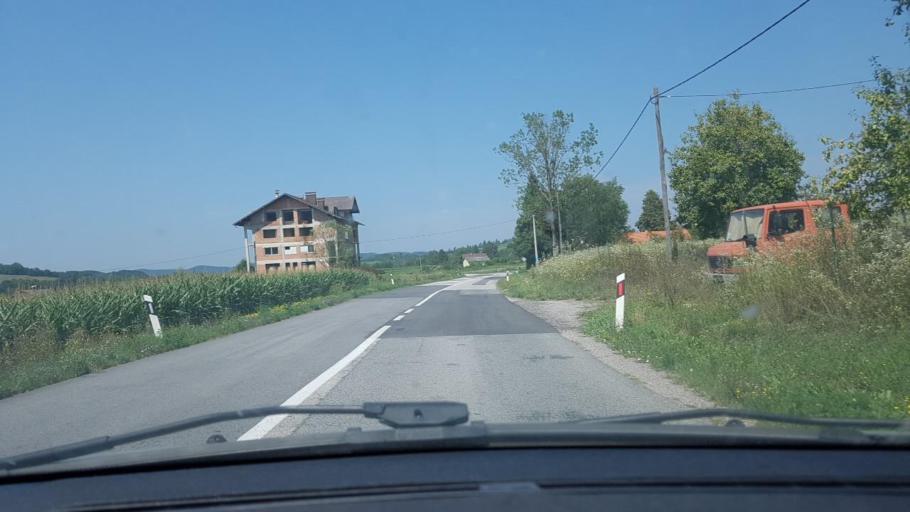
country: BA
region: Federation of Bosnia and Herzegovina
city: Velika Kladusa
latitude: 45.2143
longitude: 15.7630
